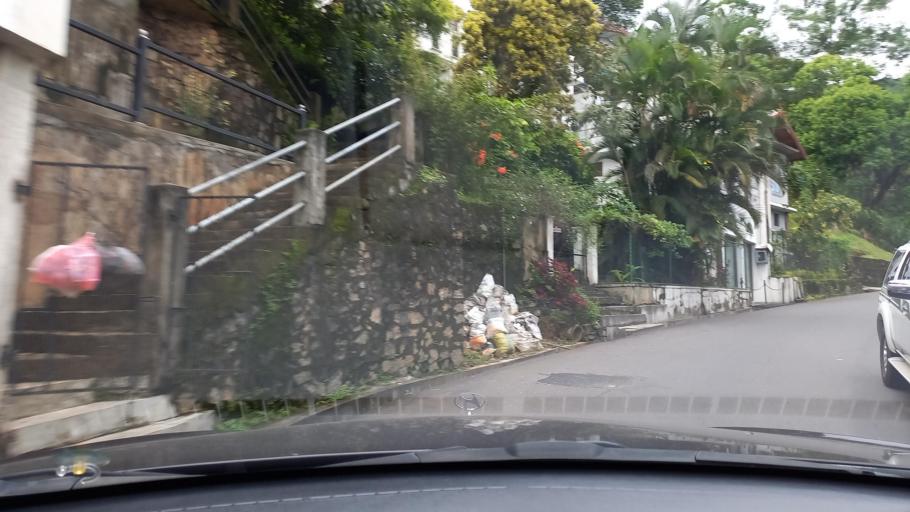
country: LK
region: Central
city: Kandy
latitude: 7.2326
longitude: 80.6050
